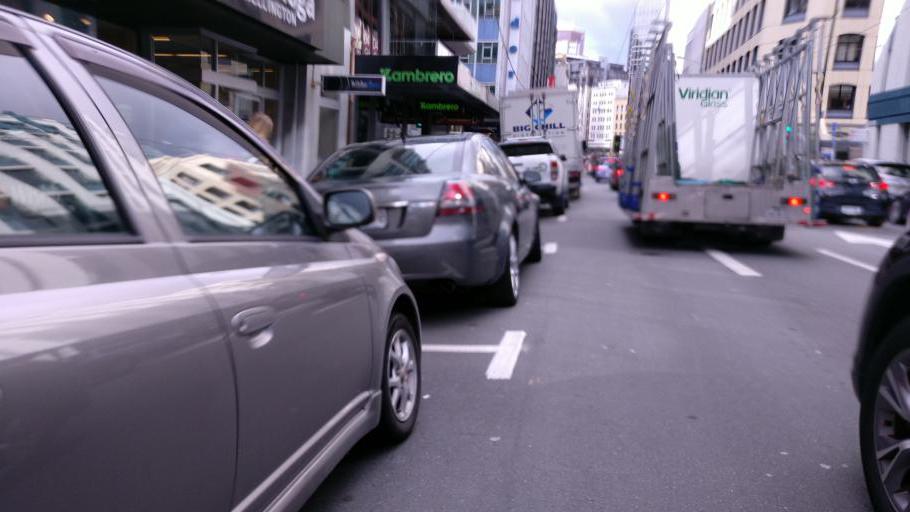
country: NZ
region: Wellington
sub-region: Wellington City
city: Wellington
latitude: -41.2830
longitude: 174.7772
